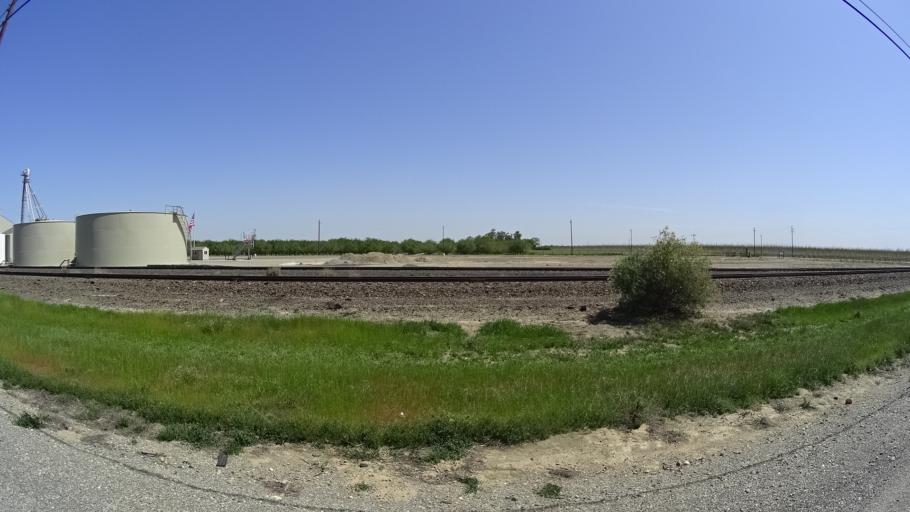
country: US
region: California
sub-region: Glenn County
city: Willows
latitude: 39.6126
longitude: -122.1941
